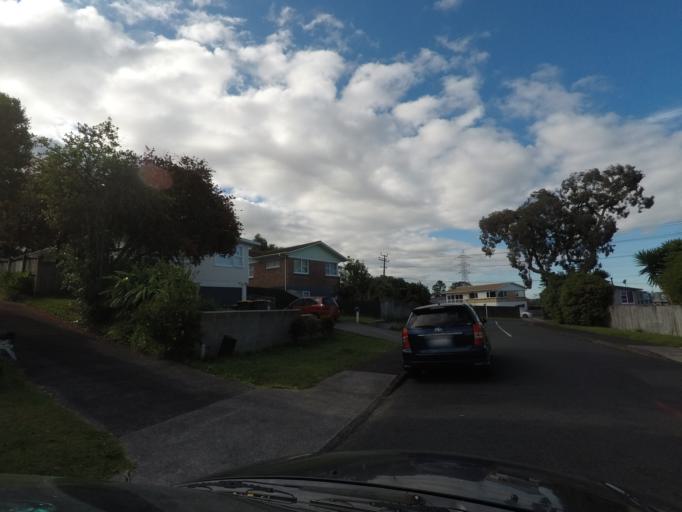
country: NZ
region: Auckland
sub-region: Auckland
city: Rosebank
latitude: -36.8801
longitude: 174.6549
